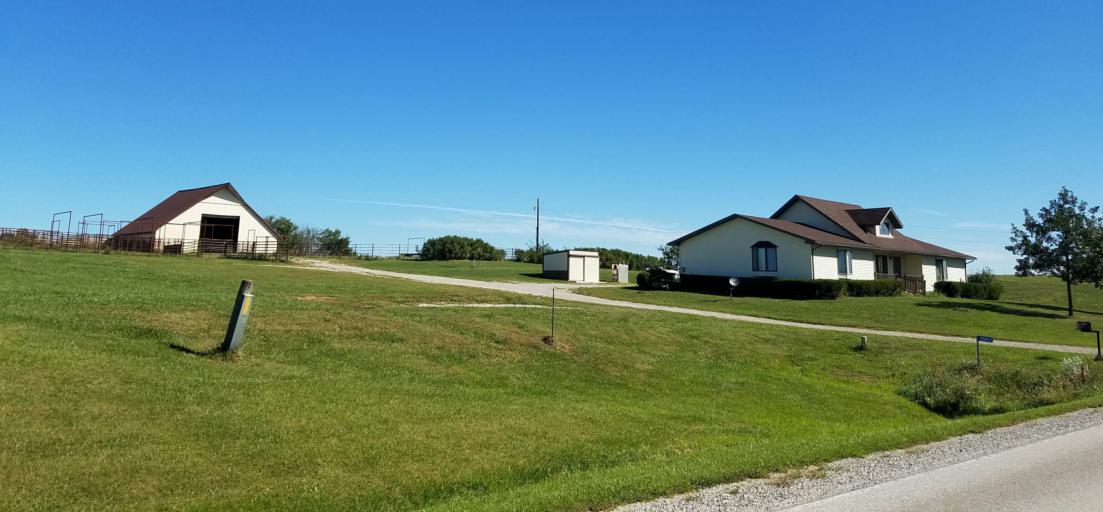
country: US
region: Iowa
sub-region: Decatur County
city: Lamoni
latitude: 40.6237
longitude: -93.8730
